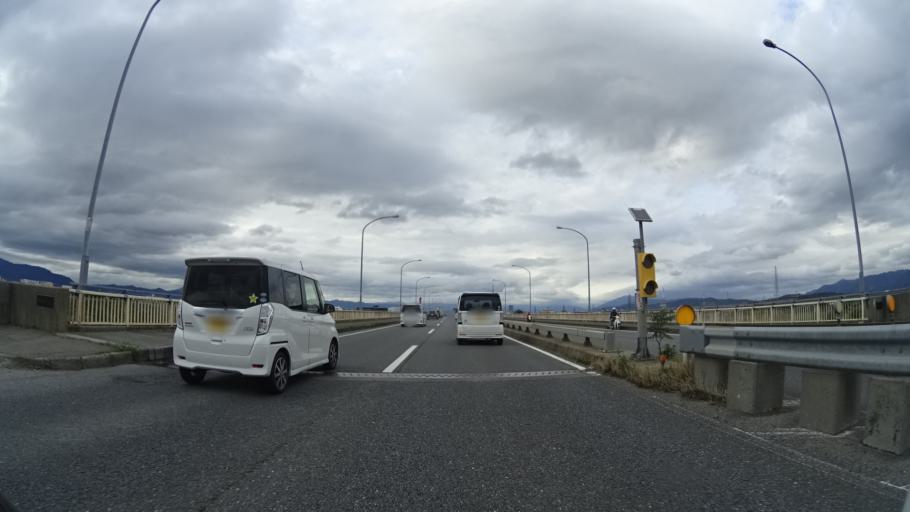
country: JP
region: Kyoto
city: Yawata
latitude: 34.9148
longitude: 135.7445
